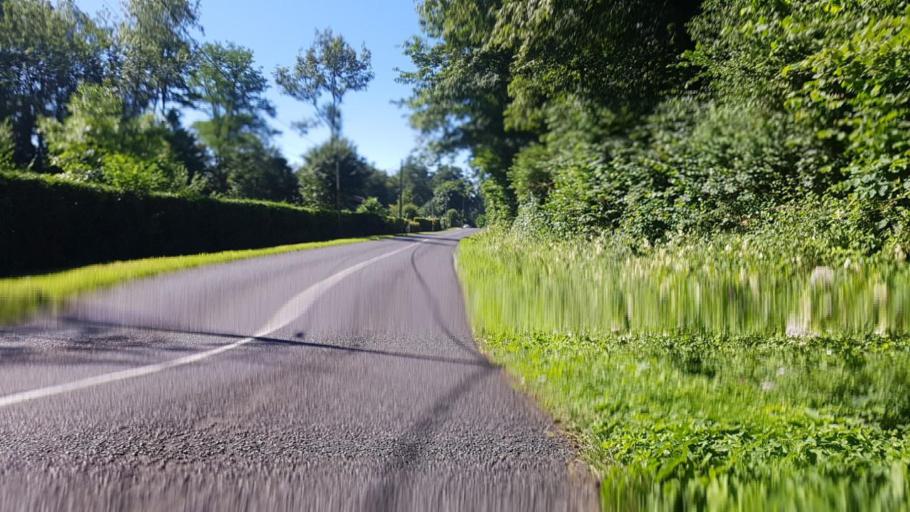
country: FR
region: Picardie
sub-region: Departement de l'Aisne
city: Chezy-sur-Marne
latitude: 48.9937
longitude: 3.3426
